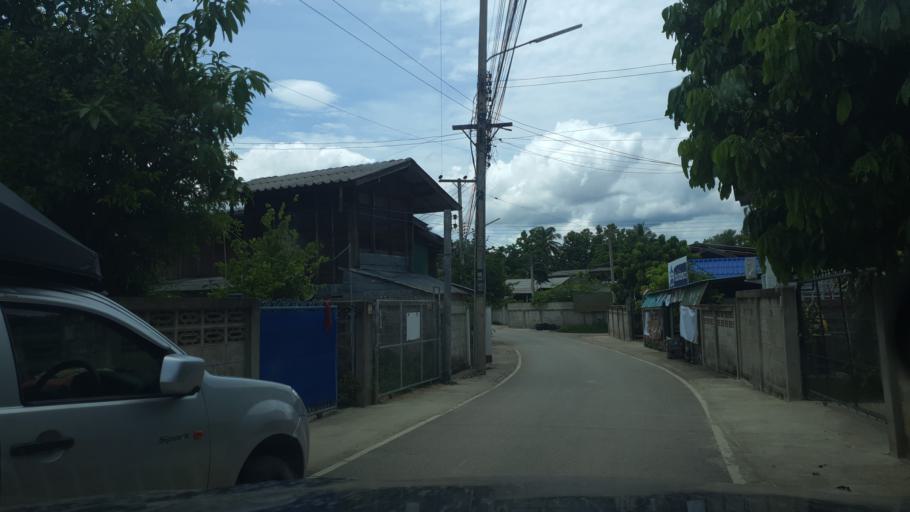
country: TH
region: Lampang
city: Sop Prap
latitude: 17.8826
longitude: 99.3826
